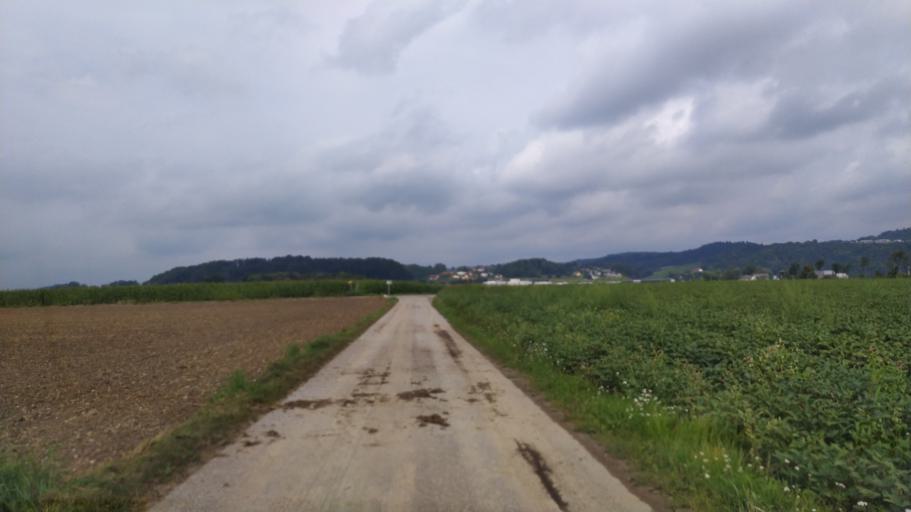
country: AT
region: Upper Austria
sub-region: Politischer Bezirk Perg
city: Bad Kreuzen
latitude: 48.2000
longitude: 14.7574
